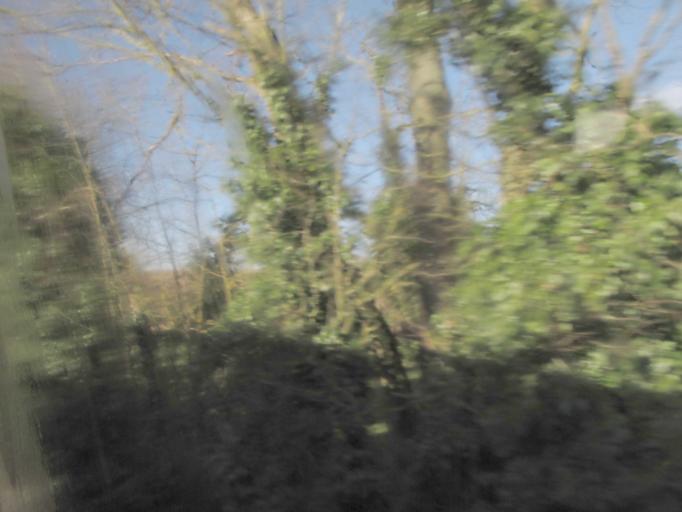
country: GB
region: England
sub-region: Hampshire
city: Kings Worthy
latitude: 51.1609
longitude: -1.3220
